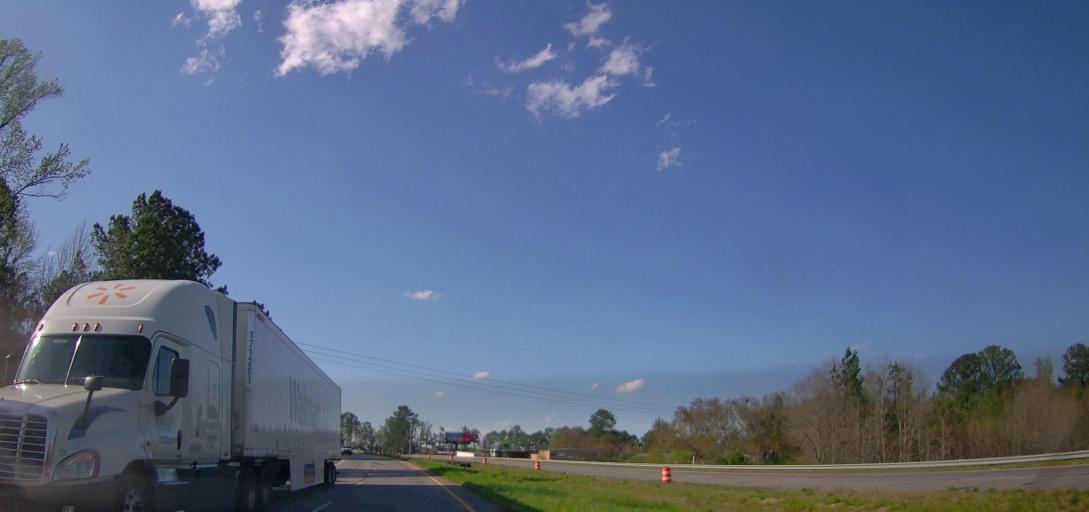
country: US
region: Georgia
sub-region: Baldwin County
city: Milledgeville
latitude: 33.0705
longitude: -83.2495
